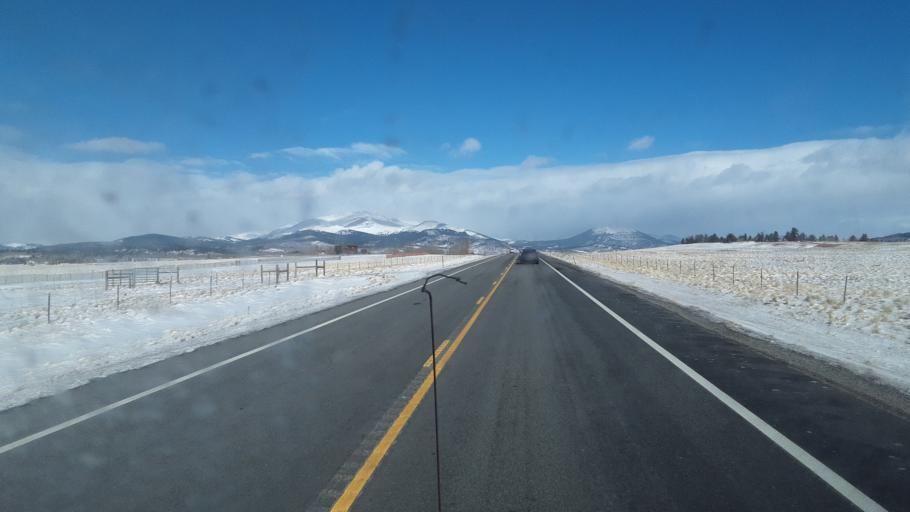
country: US
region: Colorado
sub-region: Park County
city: Fairplay
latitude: 39.1952
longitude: -105.9962
